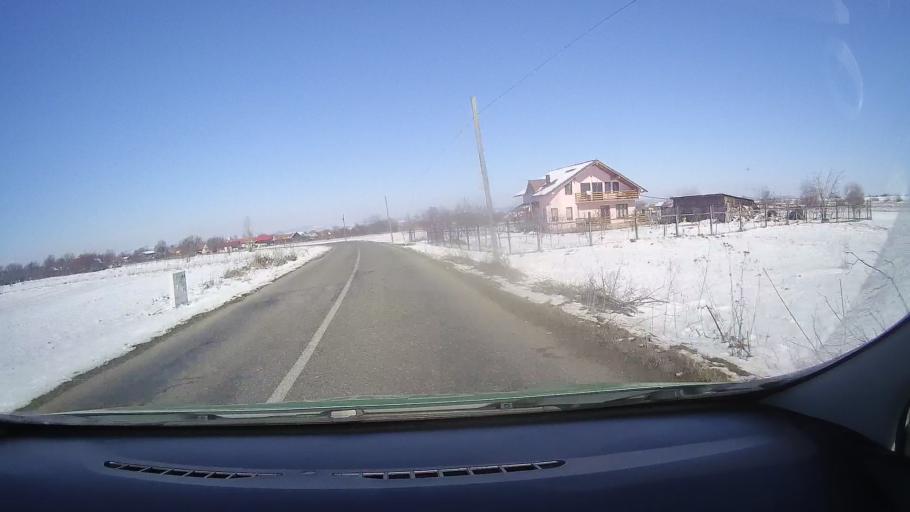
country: RO
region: Brasov
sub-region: Comuna Harseni
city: Harseni
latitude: 45.7827
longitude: 25.0014
